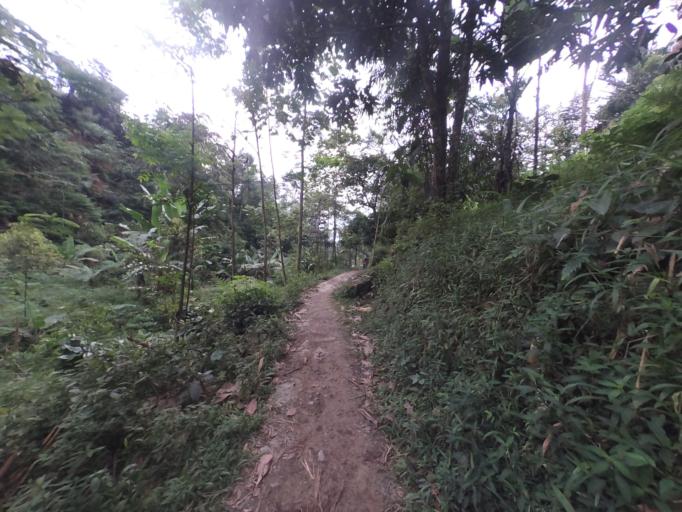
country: ID
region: West Java
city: Cicurug
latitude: -6.7069
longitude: 106.6643
